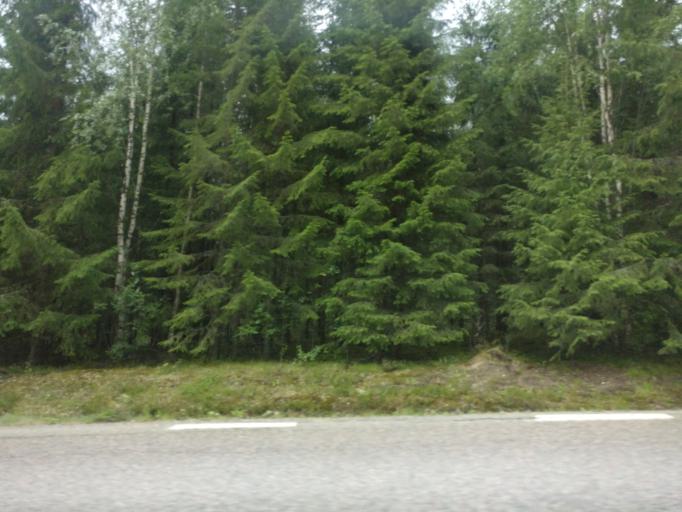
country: SE
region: Vaermland
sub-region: Torsby Kommun
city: Torsby
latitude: 60.7614
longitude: 12.7636
